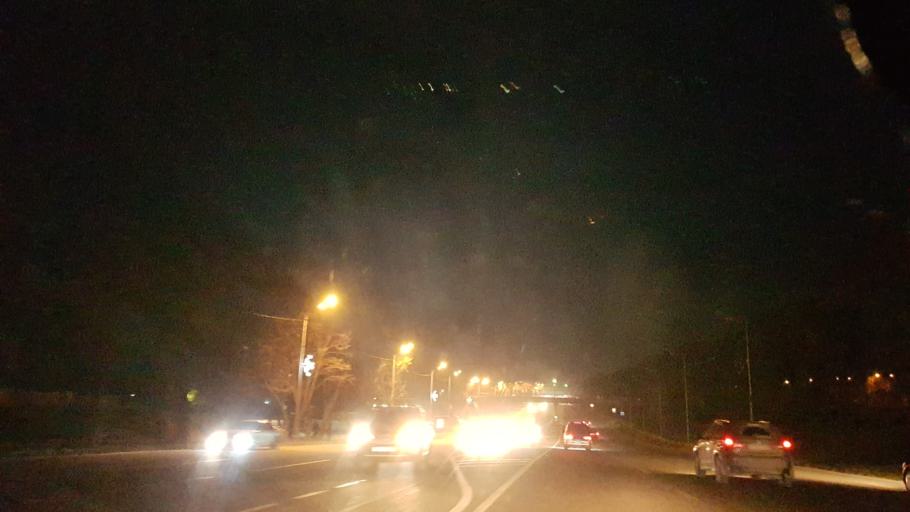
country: KZ
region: Almaty Qalasy
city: Almaty
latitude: 43.2933
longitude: 76.9715
